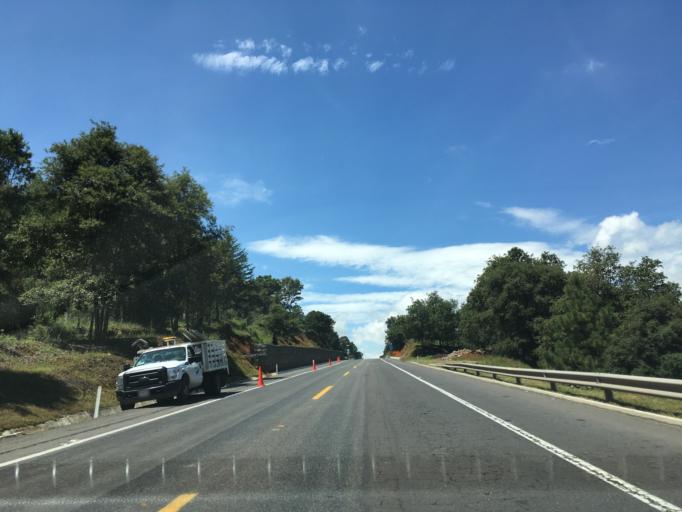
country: MX
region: Michoacan
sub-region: Patzcuaro
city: Santa Ana Chapitiro
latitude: 19.5062
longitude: -101.6771
